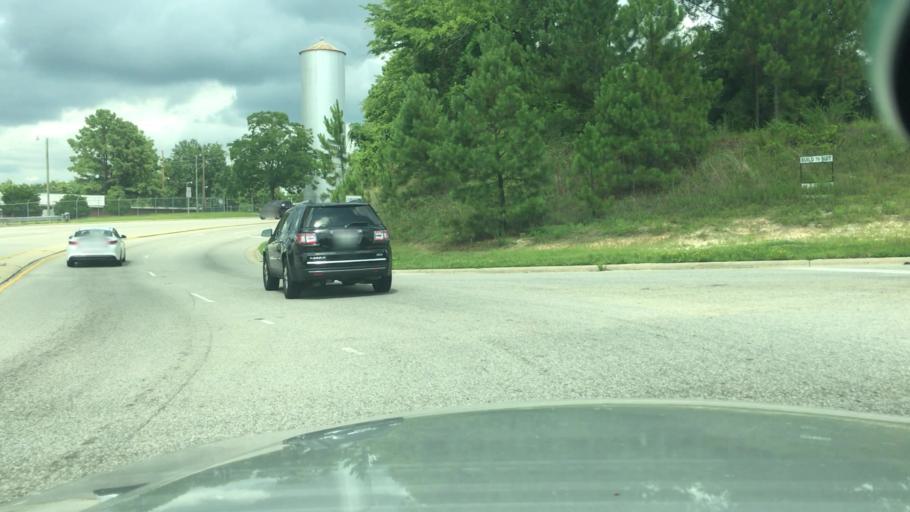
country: US
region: North Carolina
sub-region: Cumberland County
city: Hope Mills
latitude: 35.0015
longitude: -78.9759
